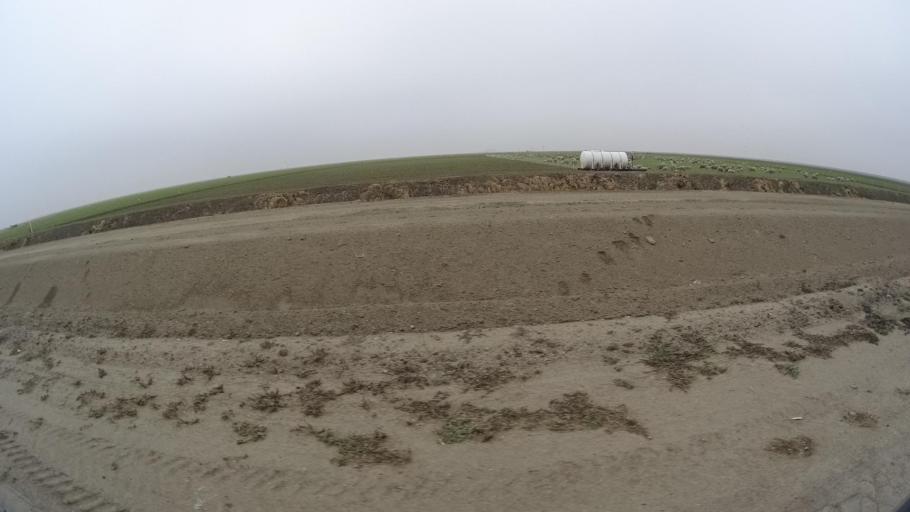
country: US
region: California
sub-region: Kern County
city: Rosedale
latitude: 35.1930
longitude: -119.1991
